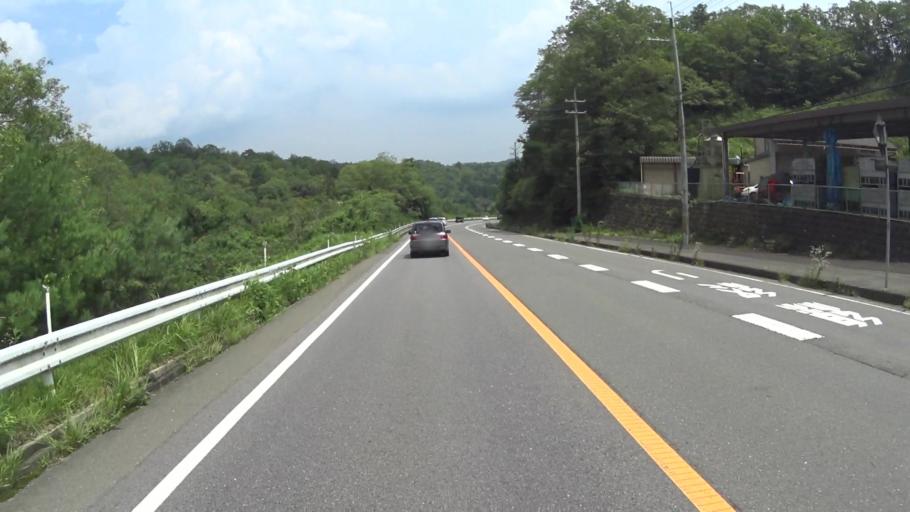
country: JP
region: Mie
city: Ueno-ebisumachi
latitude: 34.7708
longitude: 136.0205
